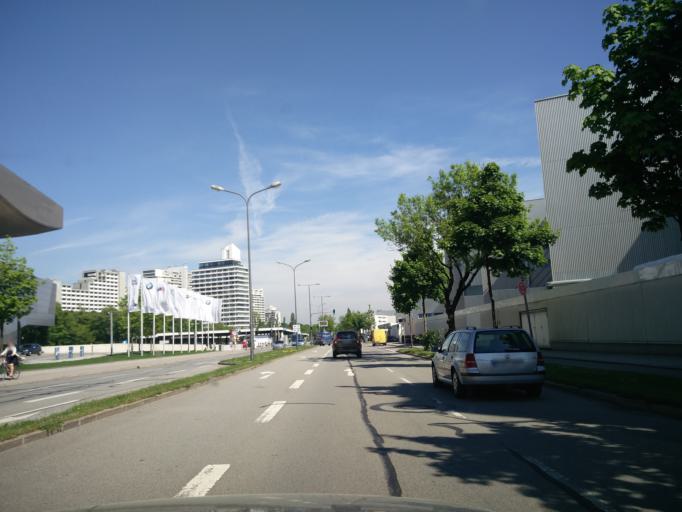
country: DE
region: Bavaria
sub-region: Upper Bavaria
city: Munich
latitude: 48.1774
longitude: 11.5576
